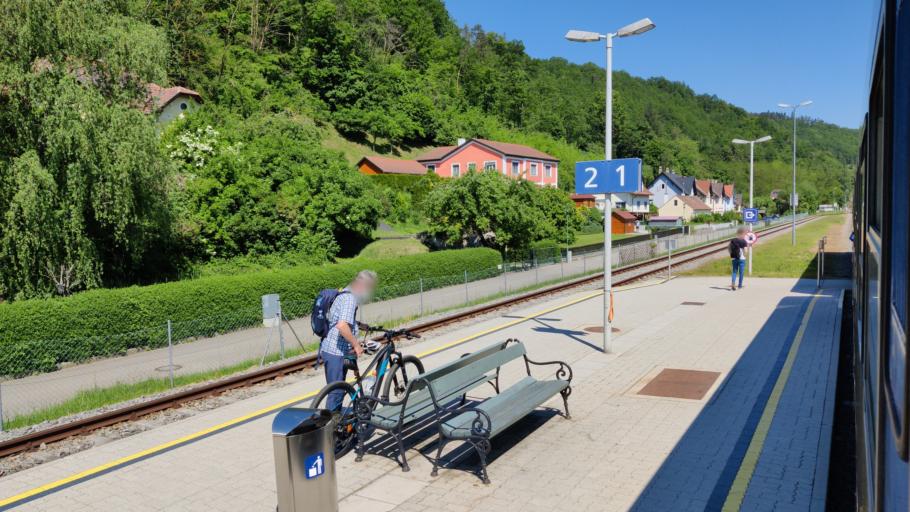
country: AT
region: Lower Austria
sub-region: Politischer Bezirk Horn
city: Gars am Kamp
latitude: 48.5975
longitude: 15.6552
